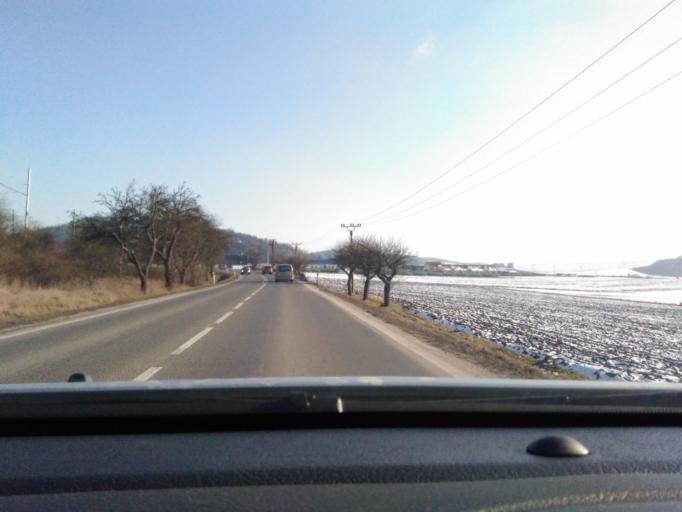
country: CZ
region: South Moravian
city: Kurim
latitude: 49.3026
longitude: 16.5138
